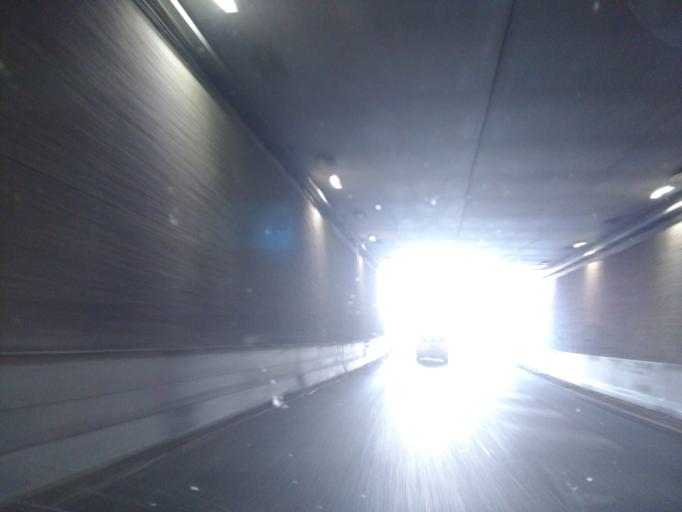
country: IT
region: Latium
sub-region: Citta metropolitana di Roma Capitale
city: Setteville
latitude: 41.9380
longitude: 12.6237
